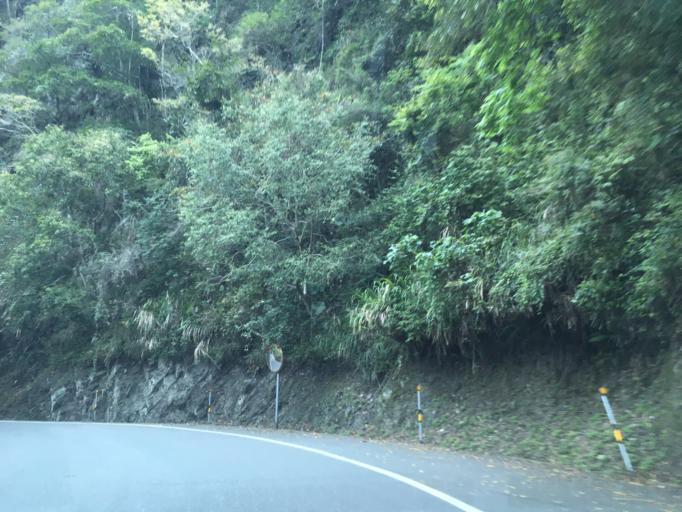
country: TW
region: Taiwan
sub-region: Hualien
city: Hualian
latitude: 24.1924
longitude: 121.4809
